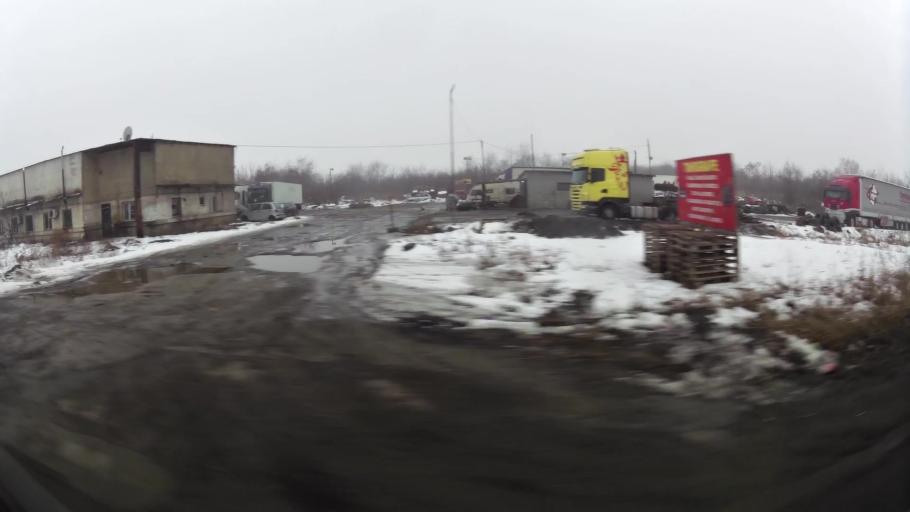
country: RO
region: Ilfov
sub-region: Comuna Clinceni
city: Olteni
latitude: 44.4025
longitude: 25.9783
